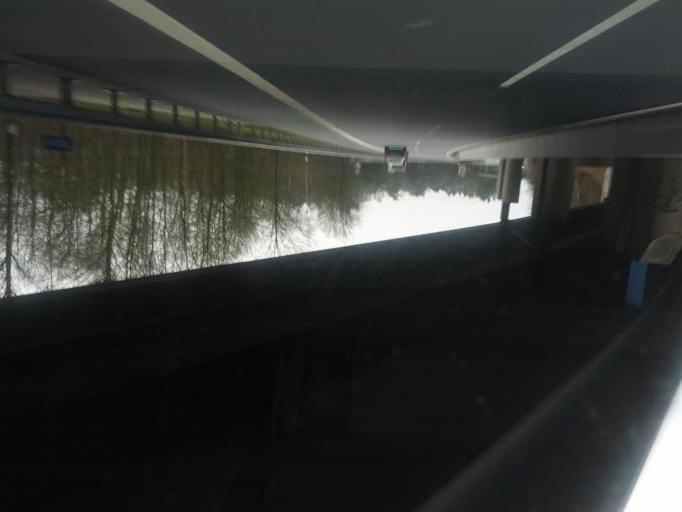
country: DE
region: Lower Saxony
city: Harmstorf
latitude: 53.3730
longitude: 10.0228
